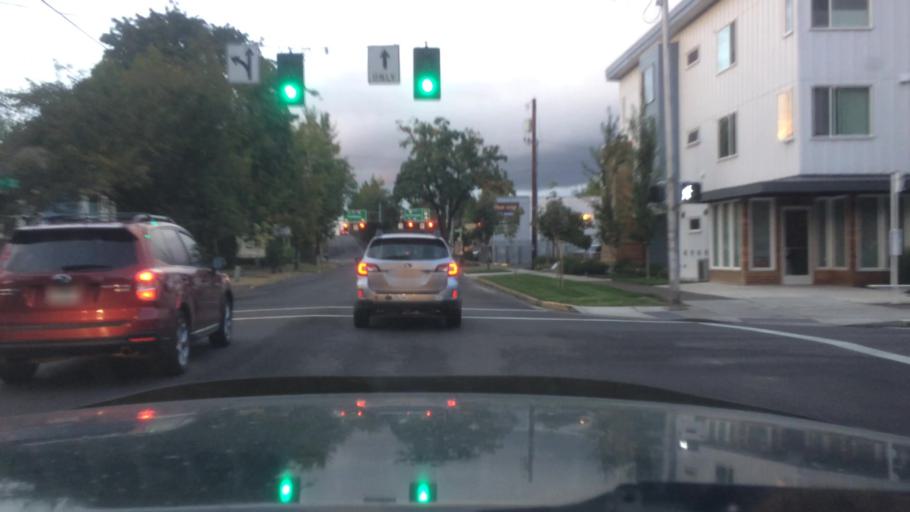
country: US
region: Oregon
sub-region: Lane County
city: Eugene
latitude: 44.0508
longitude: -123.1003
